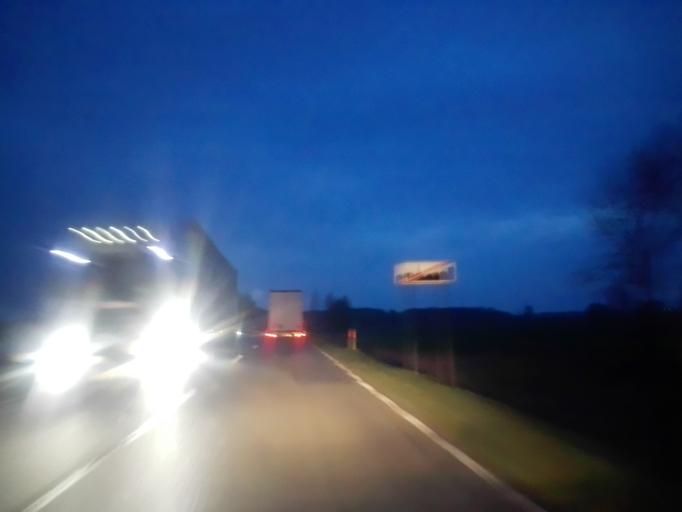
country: PL
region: Podlasie
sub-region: Powiat lomzynski
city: Sniadowo
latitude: 53.0355
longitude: 21.9798
